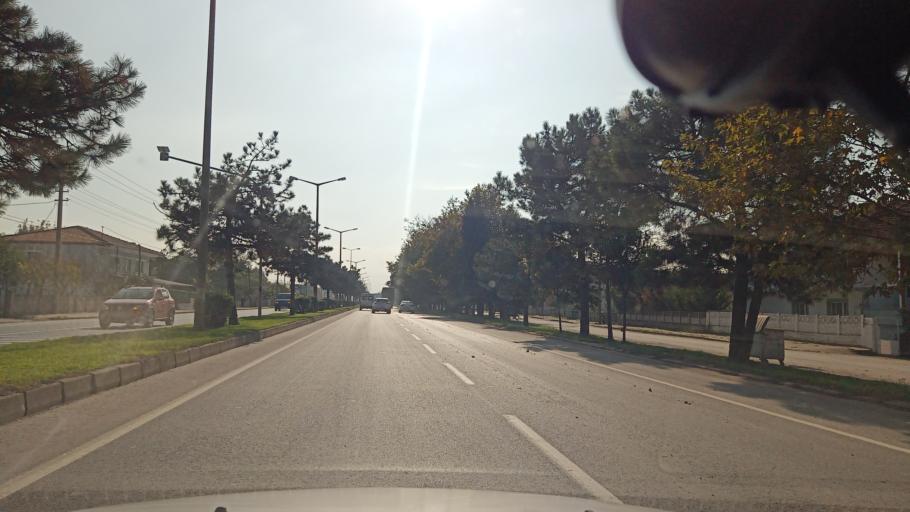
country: TR
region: Sakarya
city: Adapazari
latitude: 40.8085
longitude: 30.4054
